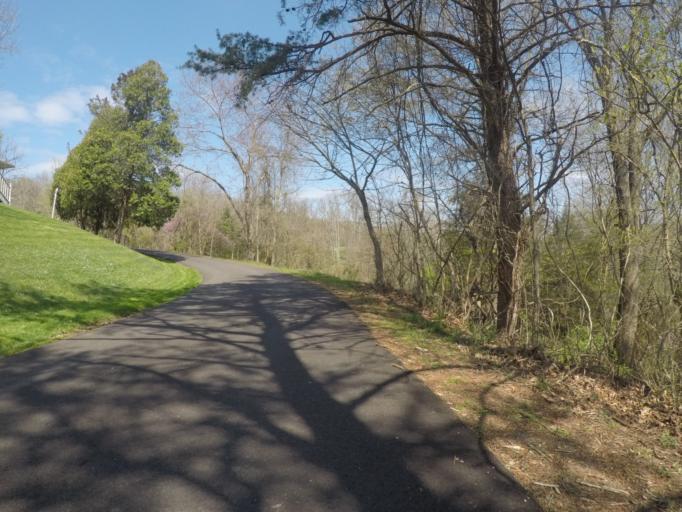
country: US
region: Ohio
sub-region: Lawrence County
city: Burlington
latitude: 38.3808
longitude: -82.5273
